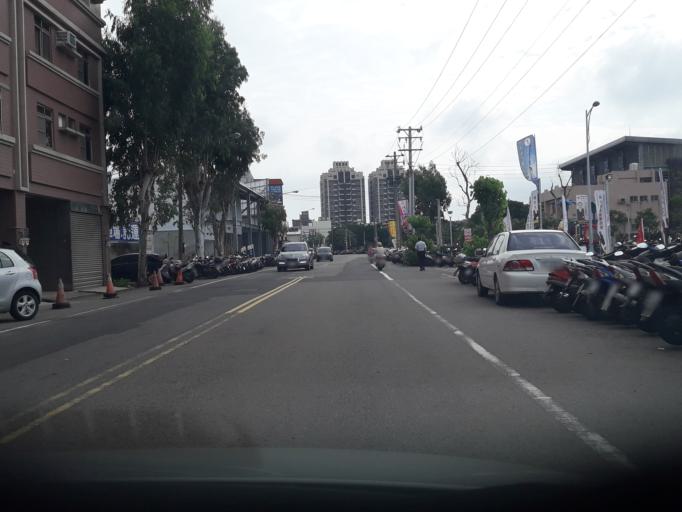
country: TW
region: Taiwan
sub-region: Miaoli
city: Miaoli
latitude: 24.6876
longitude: 120.8818
